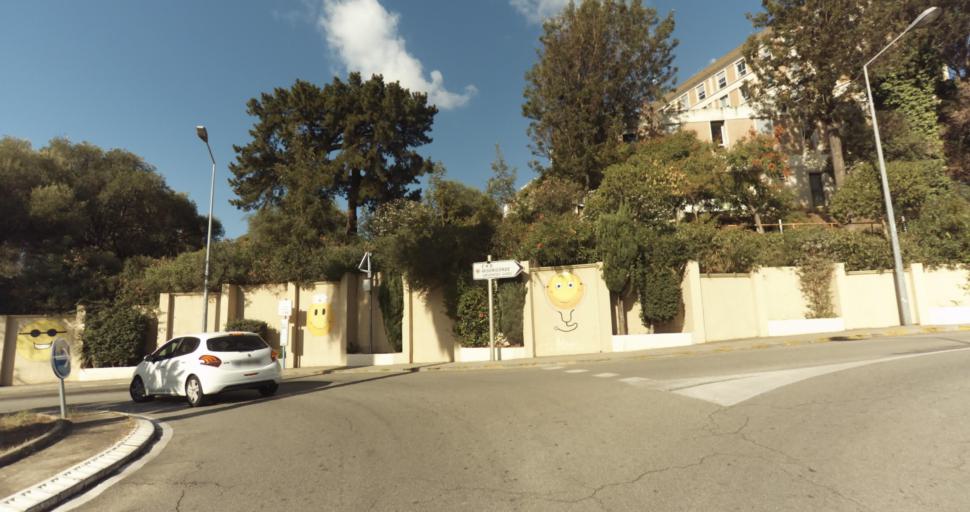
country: FR
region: Corsica
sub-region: Departement de la Corse-du-Sud
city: Ajaccio
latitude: 41.9229
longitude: 8.7353
